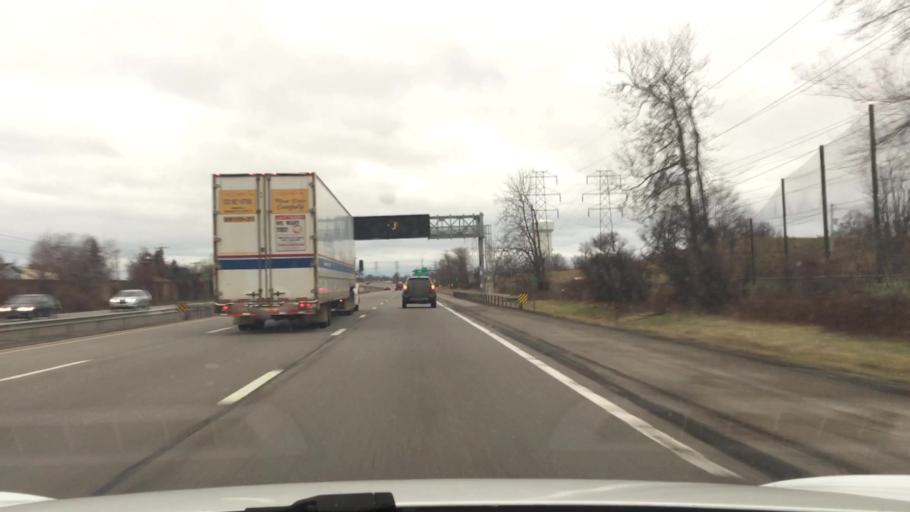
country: US
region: New York
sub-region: Erie County
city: Tonawanda
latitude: 43.0012
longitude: -78.8432
